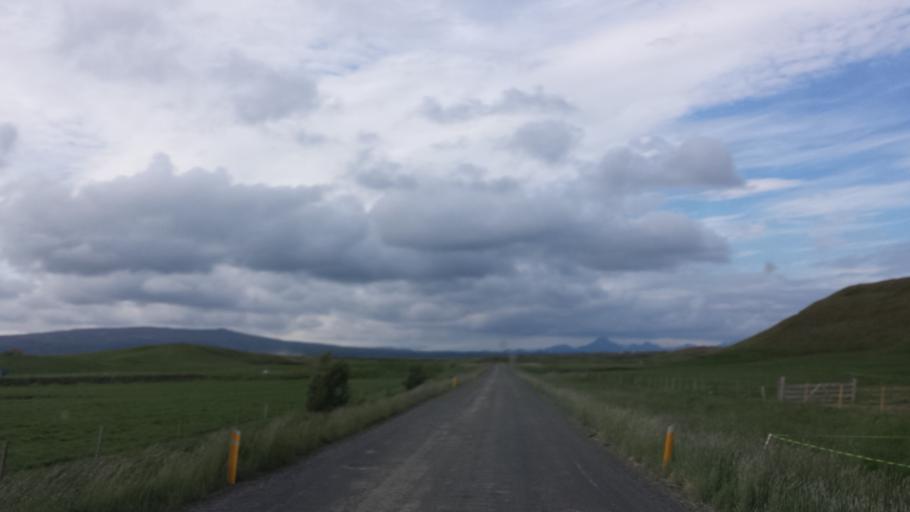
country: IS
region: South
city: Vestmannaeyjar
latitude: 64.2824
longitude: -20.2249
